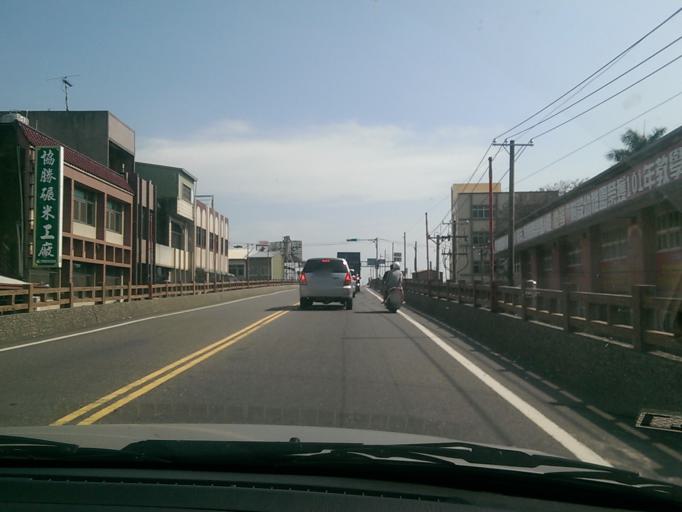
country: TW
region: Taiwan
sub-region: Chiayi
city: Taibao
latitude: 23.5657
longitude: 120.3019
